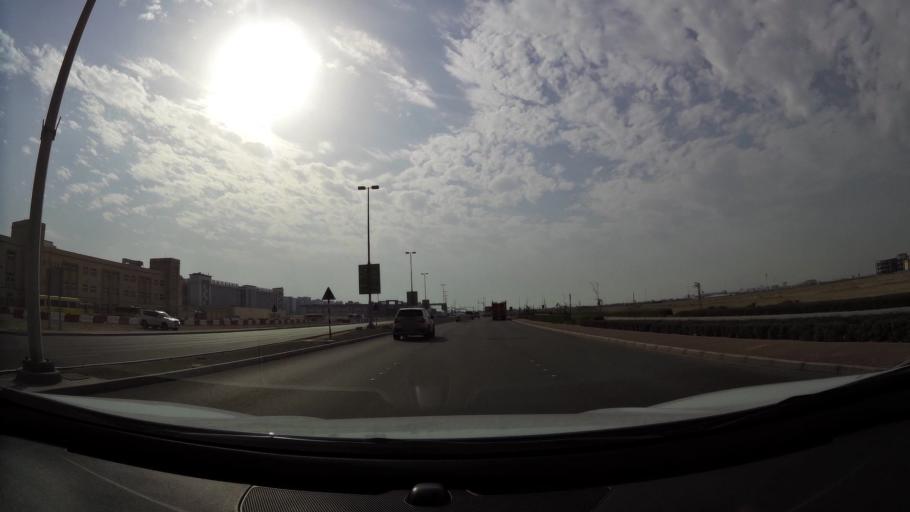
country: AE
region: Abu Dhabi
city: Abu Dhabi
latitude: 24.3475
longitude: 54.5411
